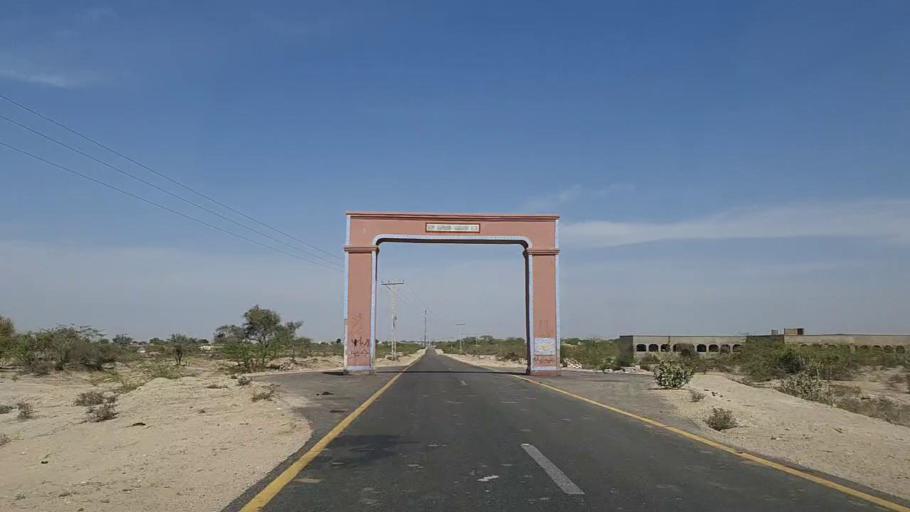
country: PK
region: Sindh
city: Mithi
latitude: 24.9675
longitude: 69.9129
